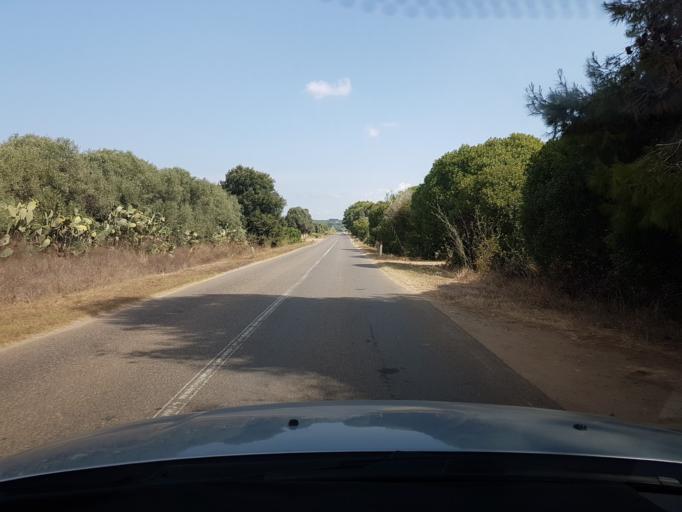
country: IT
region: Sardinia
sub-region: Provincia di Oristano
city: Cabras
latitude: 39.9019
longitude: 8.4360
